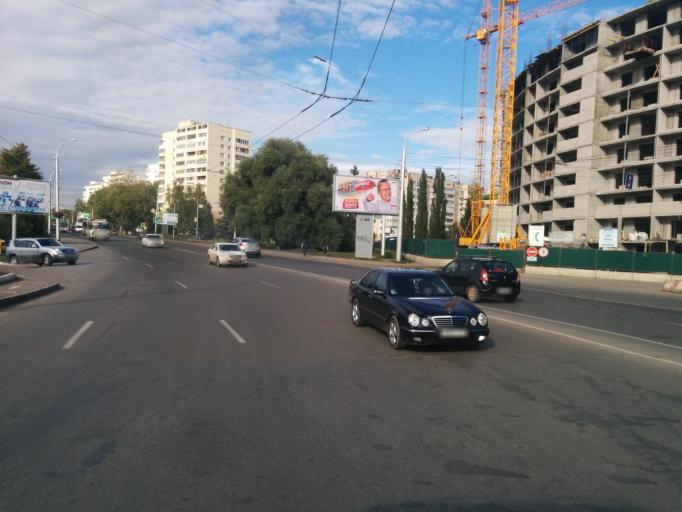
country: RU
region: Bashkortostan
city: Ufa
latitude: 54.8117
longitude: 56.0561
